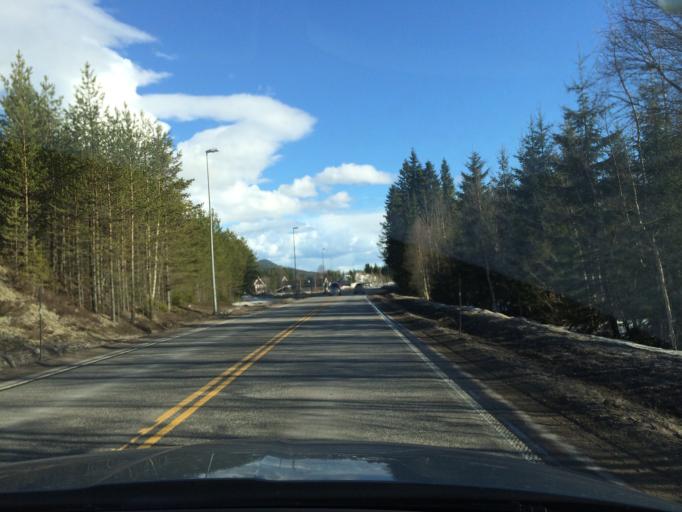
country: NO
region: Hedmark
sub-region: Trysil
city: Innbygda
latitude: 61.3174
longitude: 12.2517
